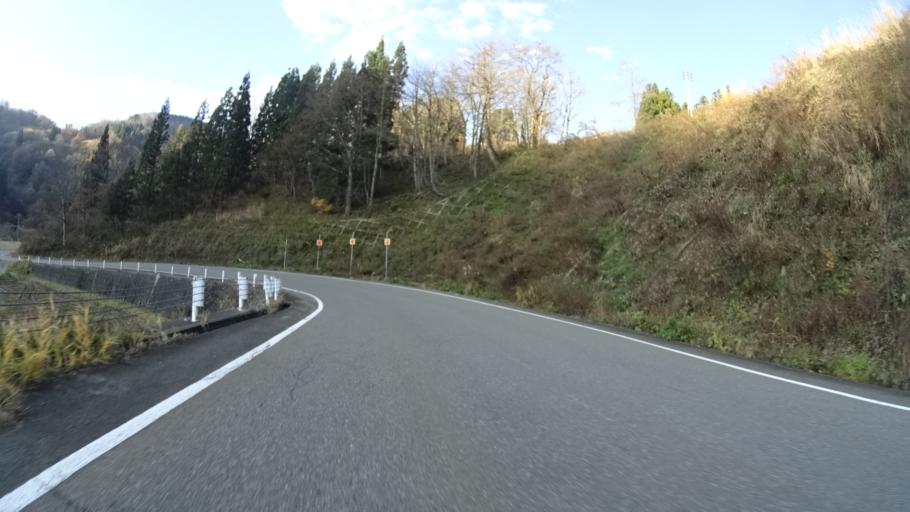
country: JP
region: Niigata
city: Shiozawa
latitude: 36.9895
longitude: 138.7624
